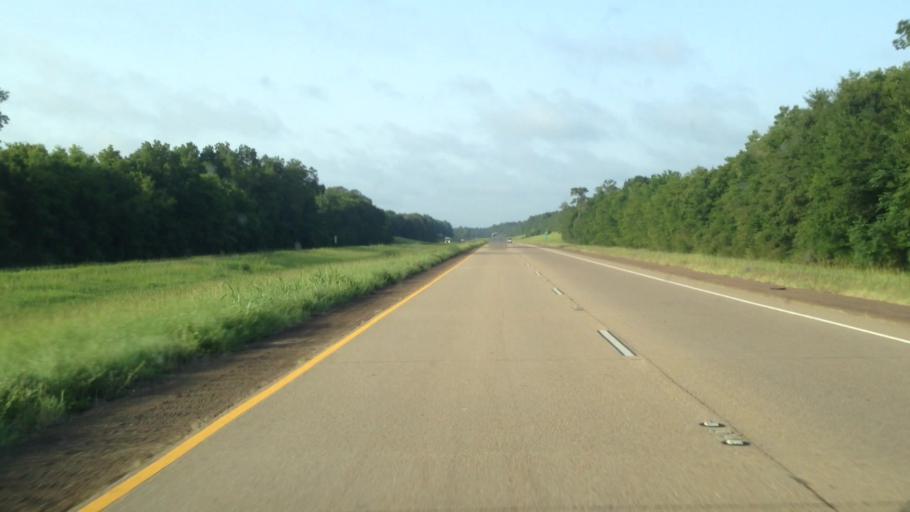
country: US
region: Louisiana
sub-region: Rapides Parish
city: Lecompte
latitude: 31.1176
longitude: -92.4429
